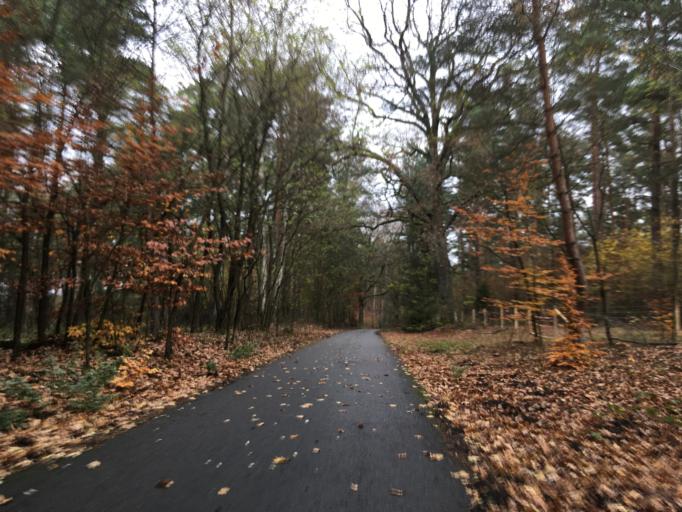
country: DE
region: Brandenburg
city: Jamlitz
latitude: 52.0400
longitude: 14.4740
